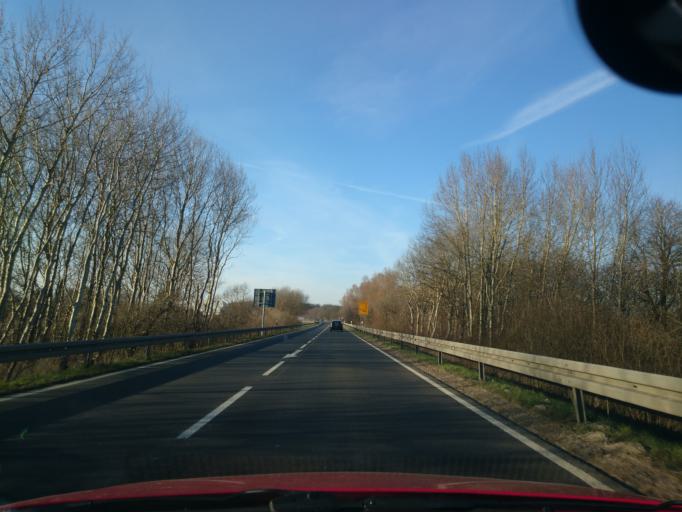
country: DE
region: Mecklenburg-Vorpommern
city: Mesekenhagen
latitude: 54.1597
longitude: 13.3090
